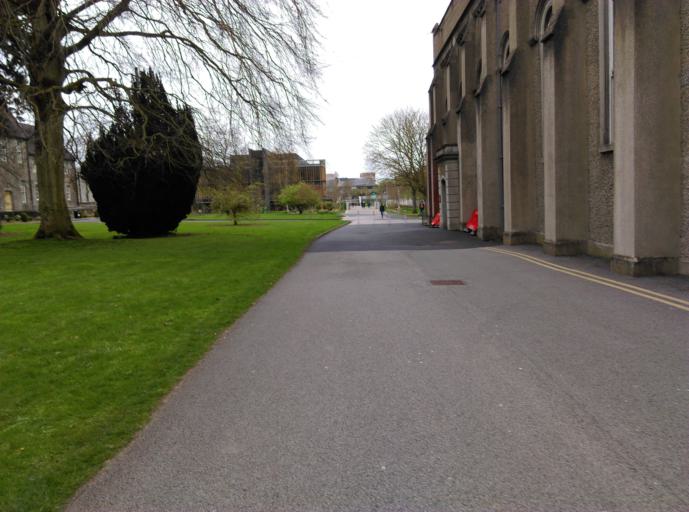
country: IE
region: Leinster
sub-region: Kildare
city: Maynooth
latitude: 53.3802
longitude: -6.5979
